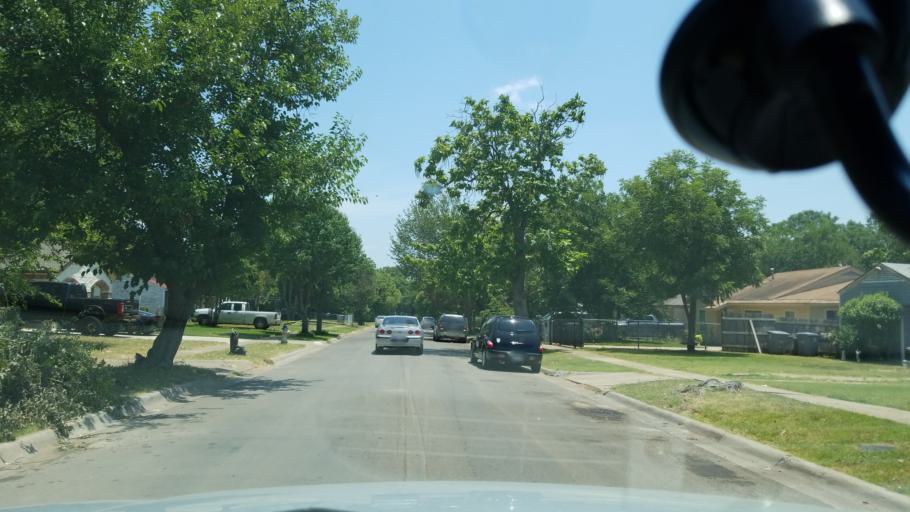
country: US
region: Texas
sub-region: Dallas County
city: Cockrell Hill
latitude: 32.7245
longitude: -96.8677
